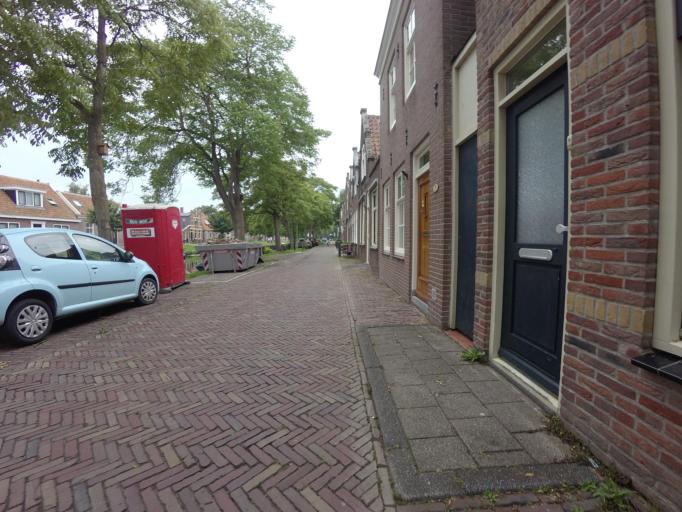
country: NL
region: North Holland
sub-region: Gemeente Enkhuizen
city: Enkhuizen
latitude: 52.7040
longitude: 5.2814
